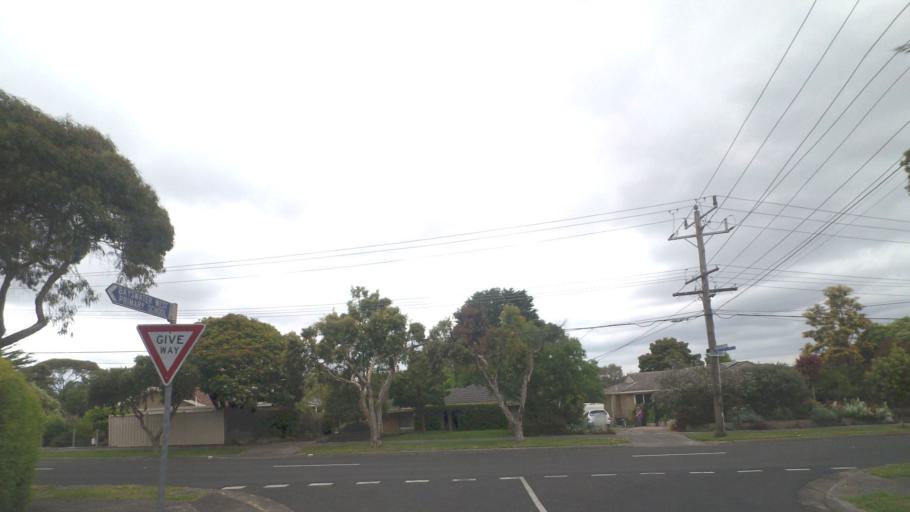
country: AU
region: Victoria
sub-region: Knox
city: Bayswater
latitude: -37.8531
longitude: 145.2529
